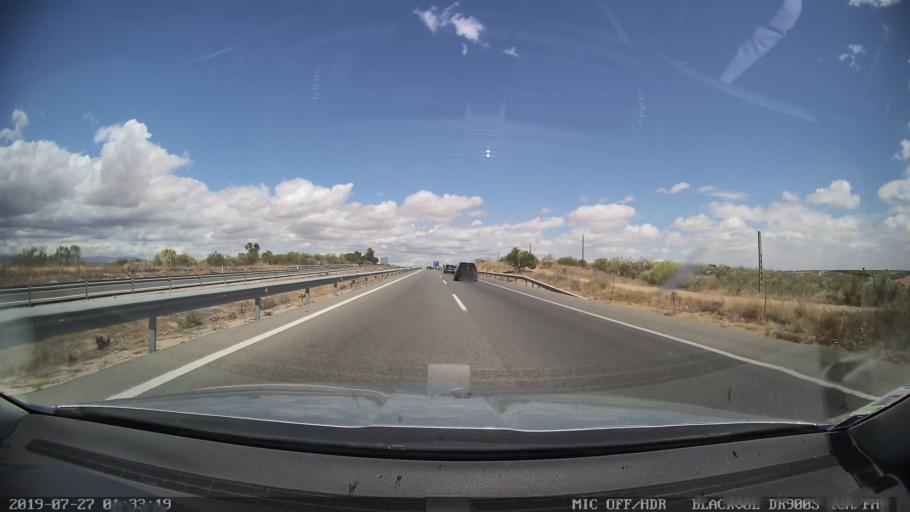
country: ES
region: Castille-La Mancha
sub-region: Province of Toledo
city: Valmojado
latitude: 40.2328
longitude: -4.0671
